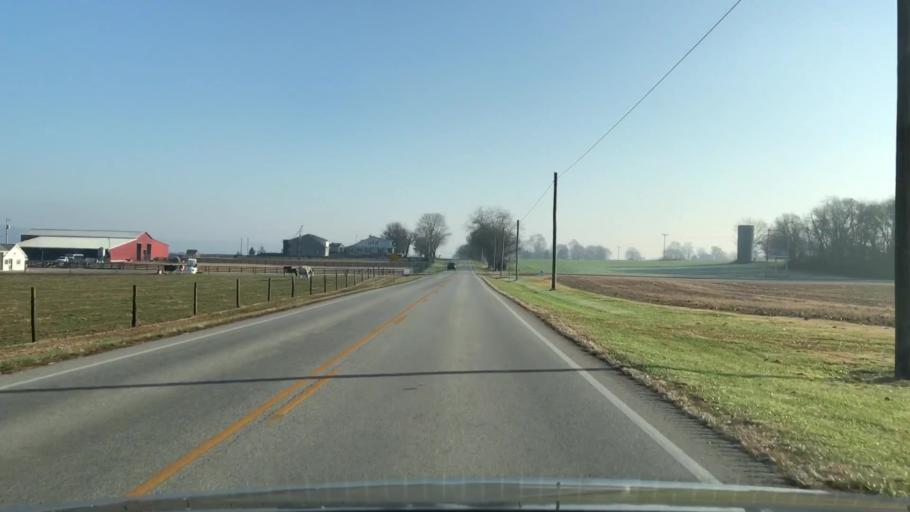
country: US
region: Kentucky
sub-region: Edmonson County
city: Brownsville
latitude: 37.0795
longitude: -86.2433
